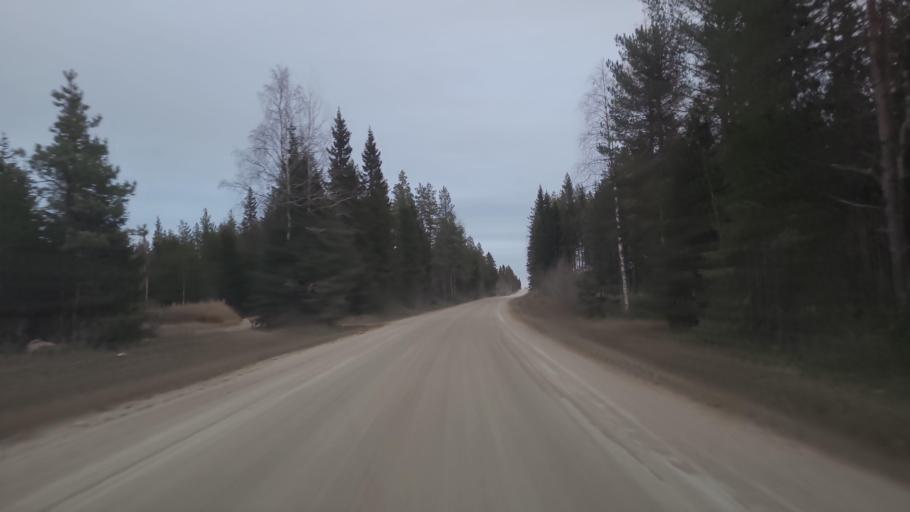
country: FI
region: Lapland
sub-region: Kemi-Tornio
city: Tervola
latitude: 66.0703
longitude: 24.8874
